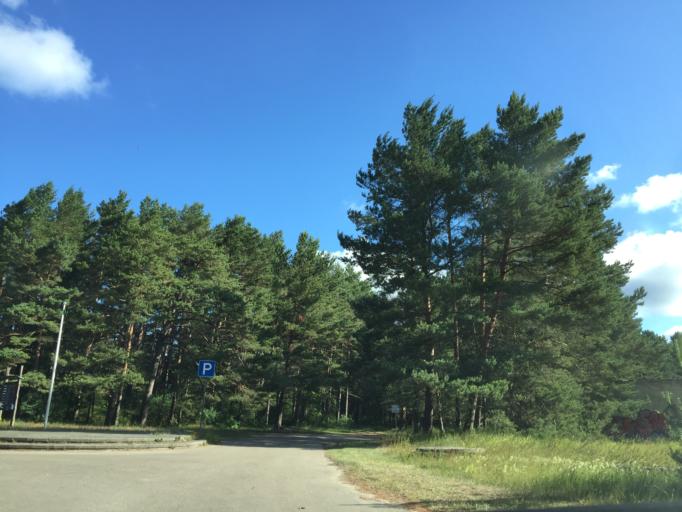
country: LV
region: Ventspils
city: Ventspils
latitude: 57.4447
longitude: 21.6057
